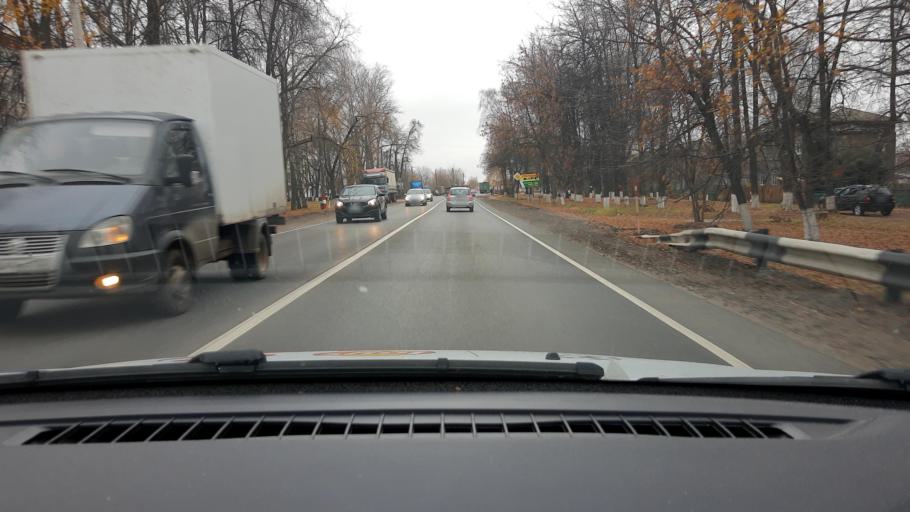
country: RU
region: Nizjnij Novgorod
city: Gidrotorf
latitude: 56.5264
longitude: 43.5539
